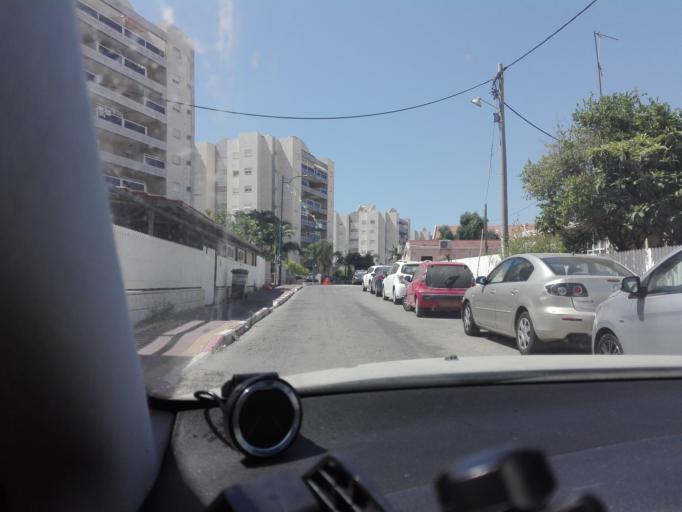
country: IL
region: Central District
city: Bene 'Ayish
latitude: 31.7314
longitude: 34.7375
